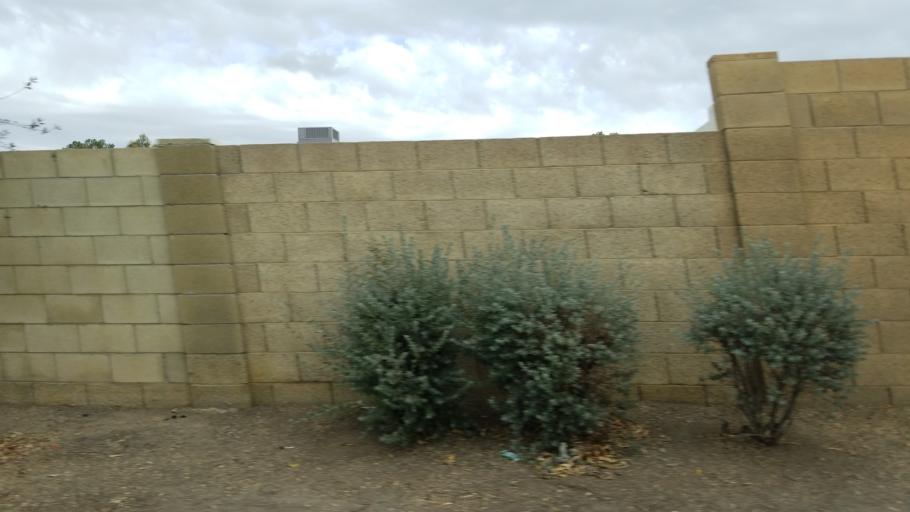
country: US
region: Arizona
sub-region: Maricopa County
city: Glendale
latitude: 33.5718
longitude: -112.1861
